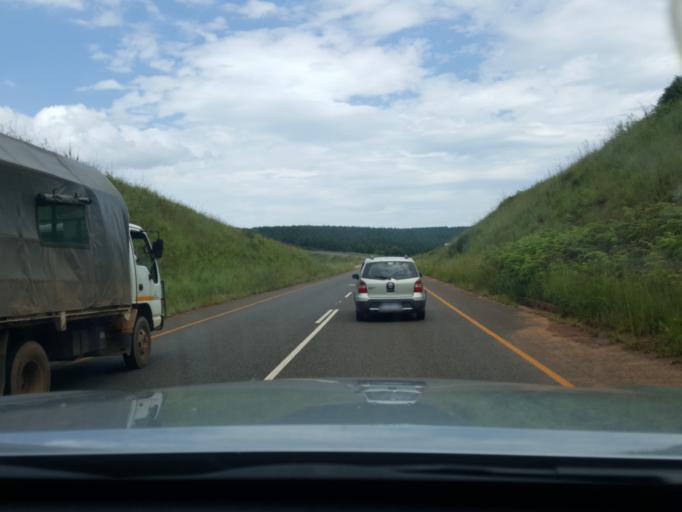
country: ZA
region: Mpumalanga
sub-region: Ehlanzeni District
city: Graksop
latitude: -25.1254
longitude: 30.8066
